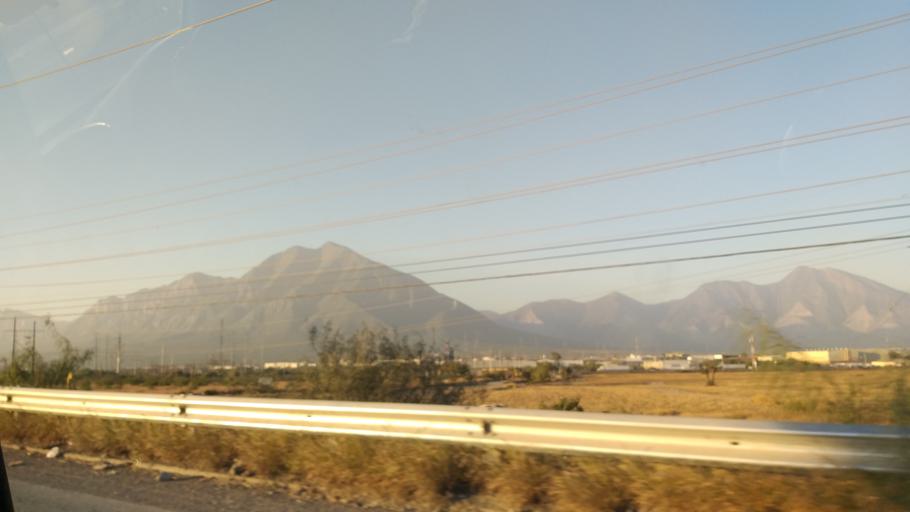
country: MX
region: Nuevo Leon
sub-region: Garcia
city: Parque Industrial Ciudad Mitras
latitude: 25.7775
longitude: -100.4428
